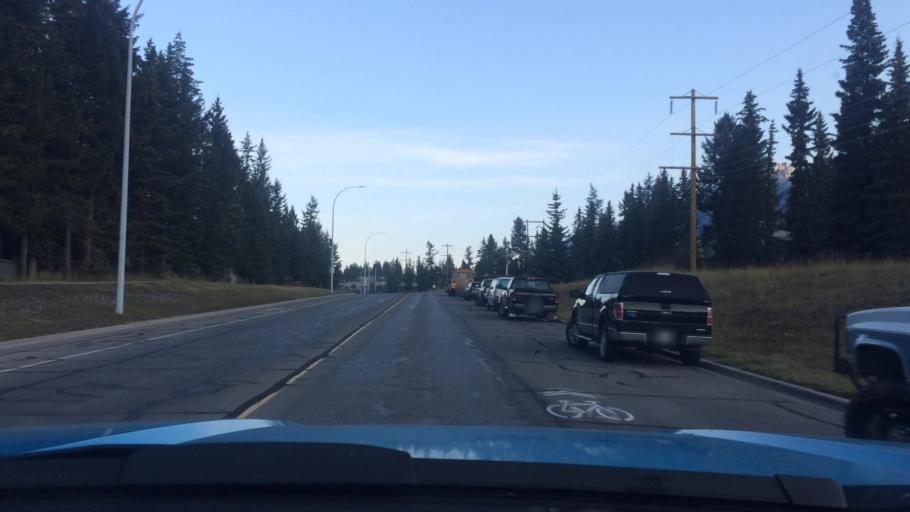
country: CA
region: Alberta
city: Canmore
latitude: 51.0834
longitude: -115.3236
